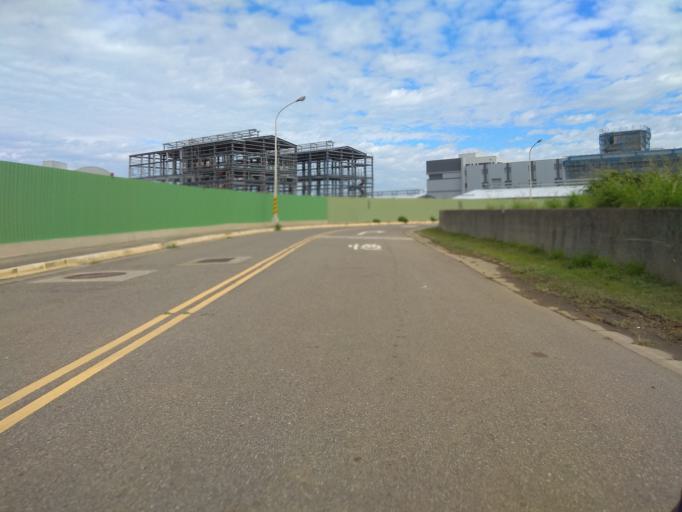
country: TW
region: Taiwan
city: Taoyuan City
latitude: 25.0488
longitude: 121.0902
